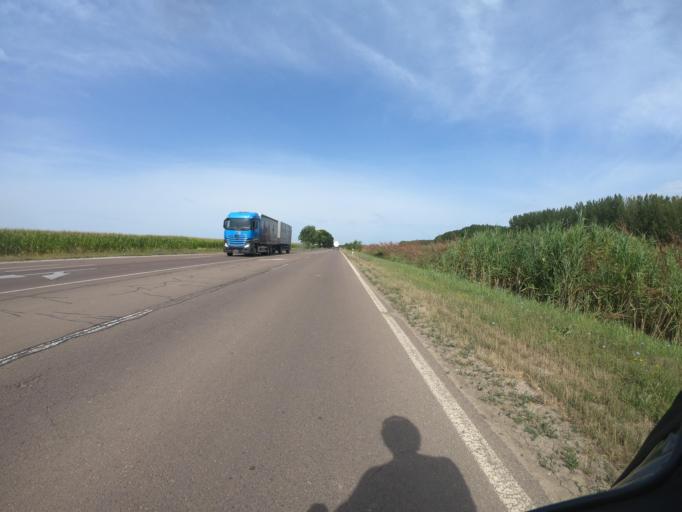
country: HU
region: Jasz-Nagykun-Szolnok
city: Tiszafured
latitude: 47.5984
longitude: 20.8138
